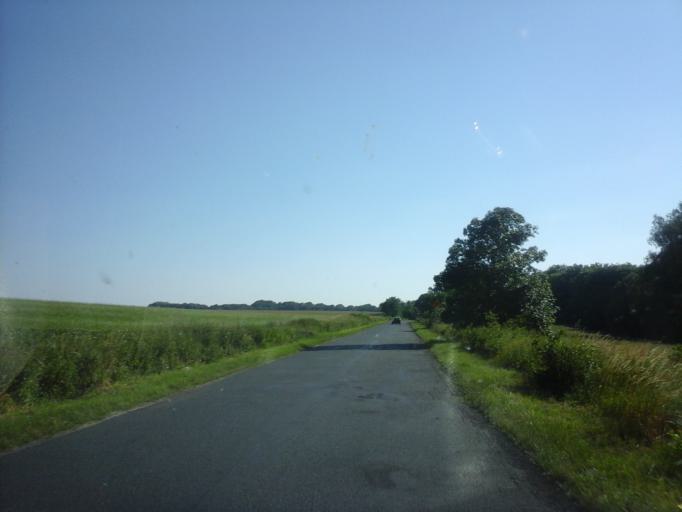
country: PL
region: West Pomeranian Voivodeship
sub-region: Powiat goleniowski
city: Nowogard
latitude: 53.6698
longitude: 15.1969
